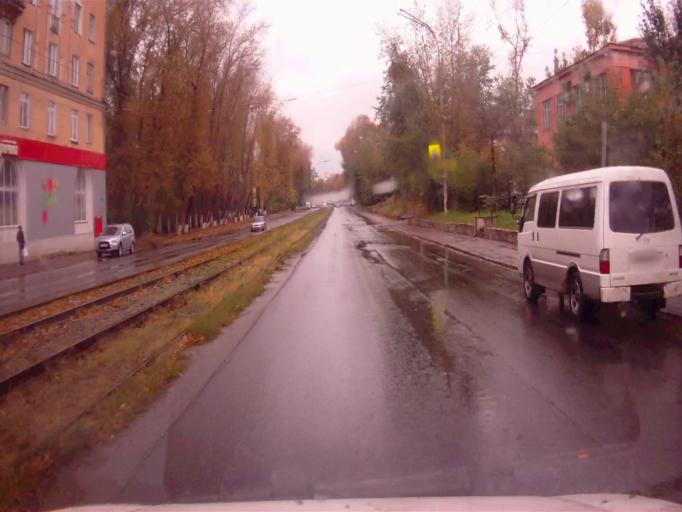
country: RU
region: Chelyabinsk
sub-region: Gorod Chelyabinsk
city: Chelyabinsk
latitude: 55.1883
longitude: 61.4132
